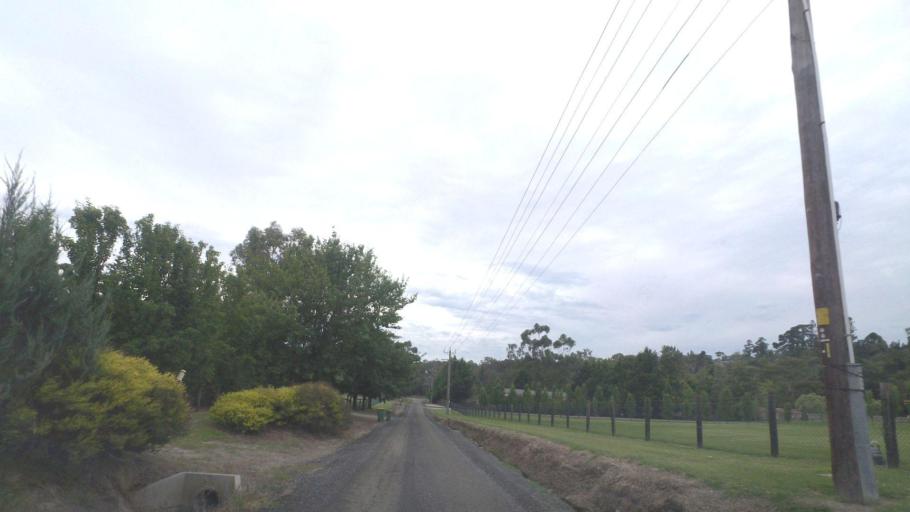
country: AU
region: Victoria
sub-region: Yarra Ranges
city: Lilydale
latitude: -37.7536
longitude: 145.3756
